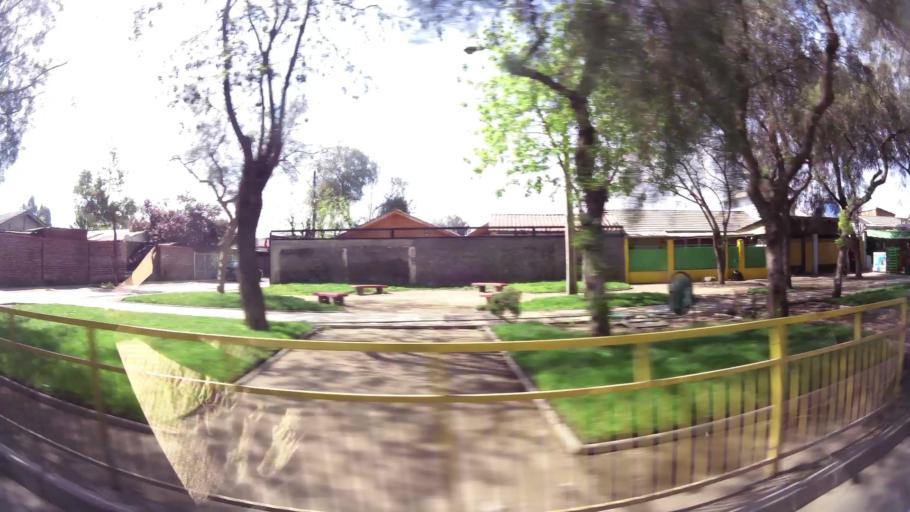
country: CL
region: Santiago Metropolitan
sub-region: Provincia de Santiago
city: Lo Prado
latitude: -33.4338
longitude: -70.7626
